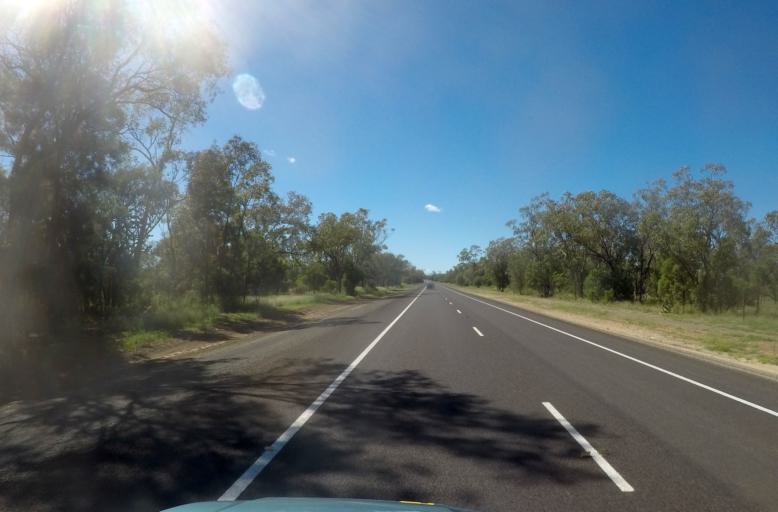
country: AU
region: Queensland
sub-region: Maranoa
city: Roma
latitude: -26.5842
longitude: 148.9777
